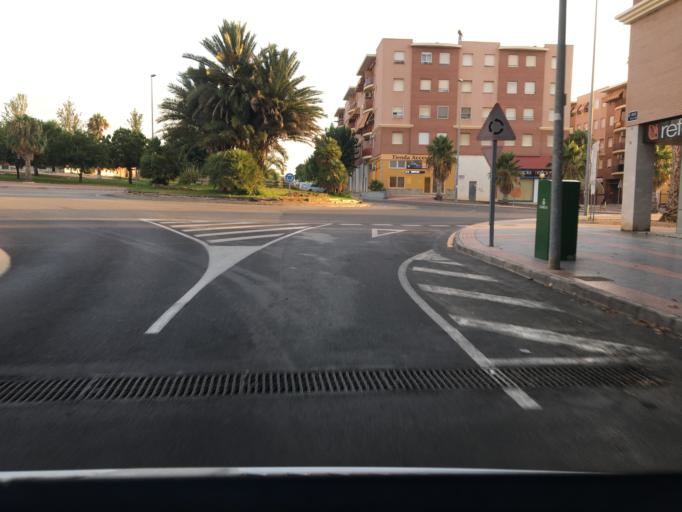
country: ES
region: Murcia
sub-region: Murcia
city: Cartagena
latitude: 37.6271
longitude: -0.9836
